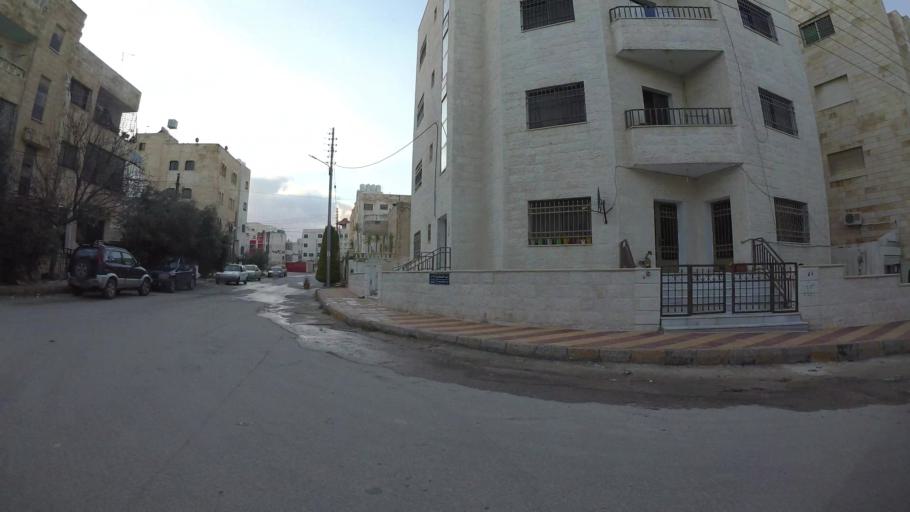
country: JO
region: Amman
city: Al Bunayyat ash Shamaliyah
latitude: 31.9167
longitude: 35.8950
